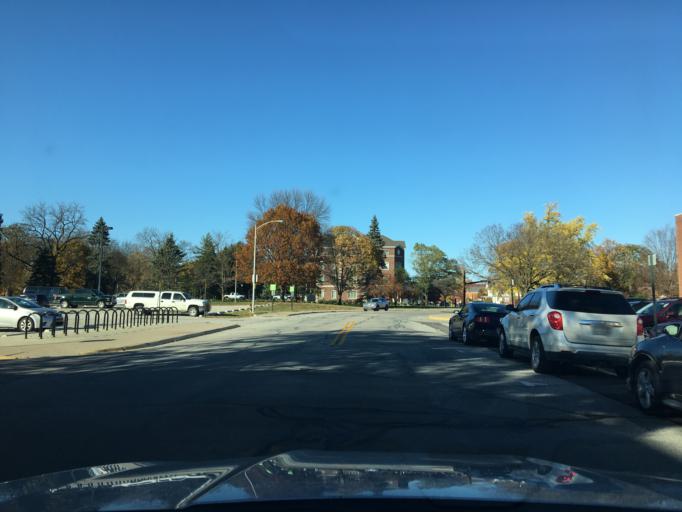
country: US
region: Indiana
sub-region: Tippecanoe County
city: West Lafayette
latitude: 40.4231
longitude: -86.9194
